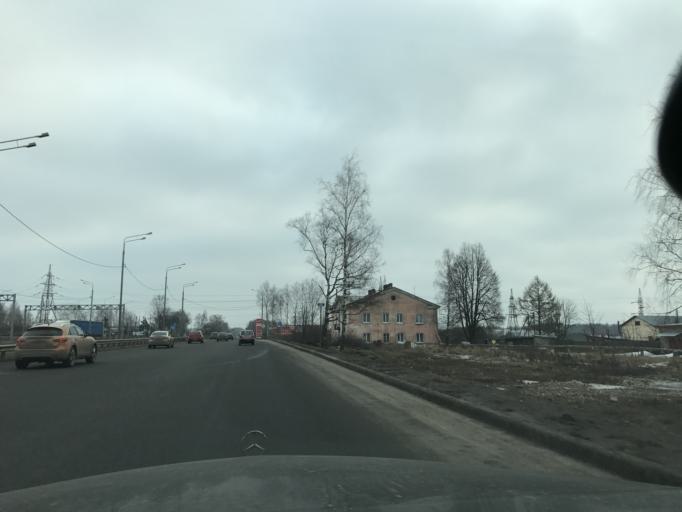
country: RU
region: Vladimir
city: Sobinka
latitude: 56.0279
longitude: 40.0035
